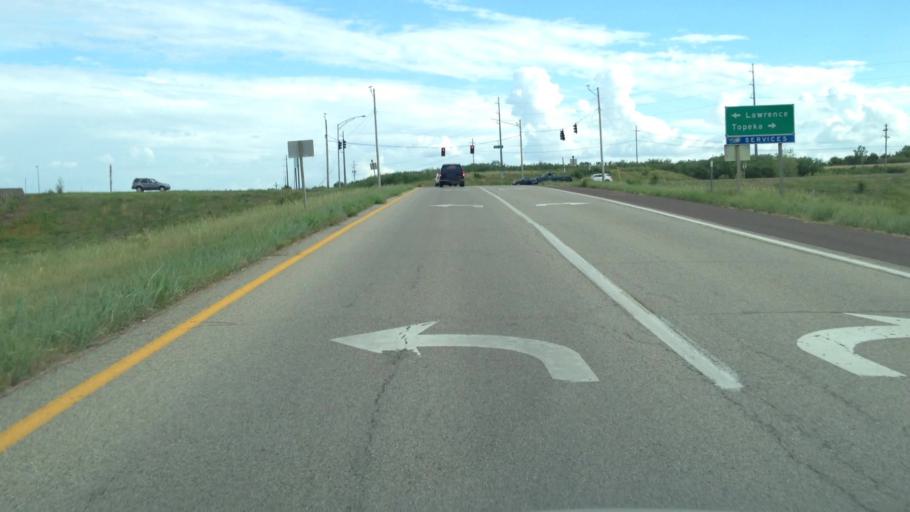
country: US
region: Kansas
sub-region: Douglas County
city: Lawrence
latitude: 38.9726
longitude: -95.3354
